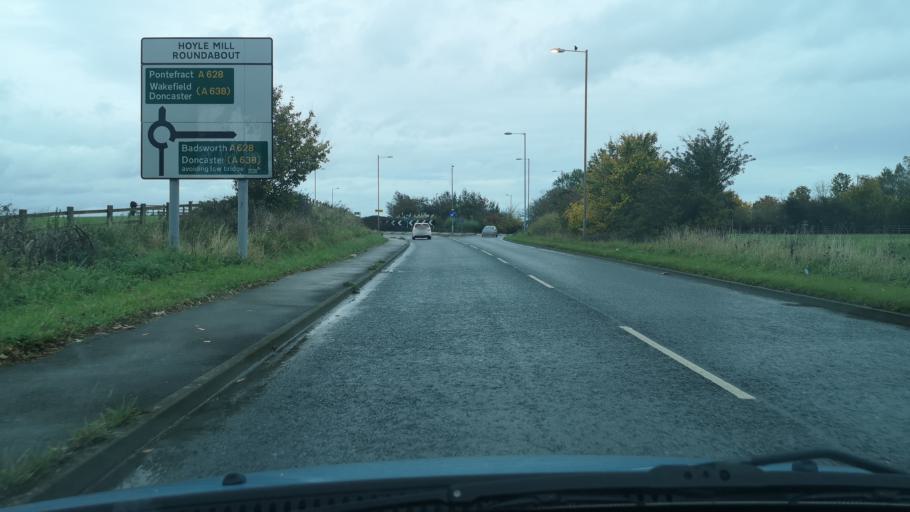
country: GB
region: England
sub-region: City and Borough of Wakefield
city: Hemsworth
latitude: 53.6265
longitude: -1.3396
